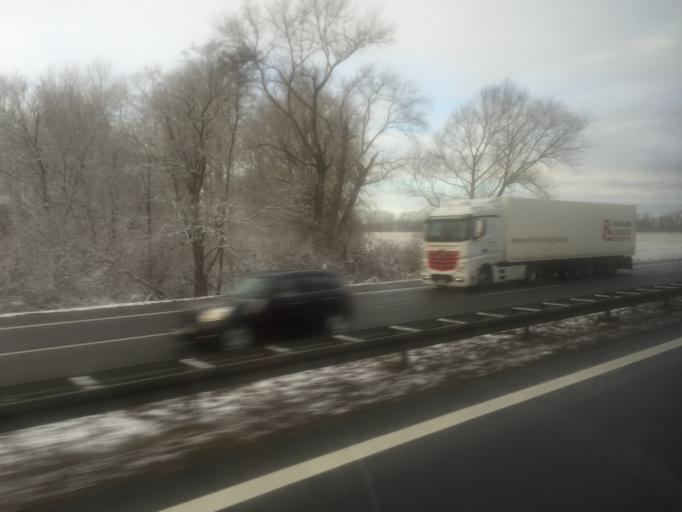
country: DE
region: Brandenburg
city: Fehrbellin
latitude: 52.8115
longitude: 12.7943
